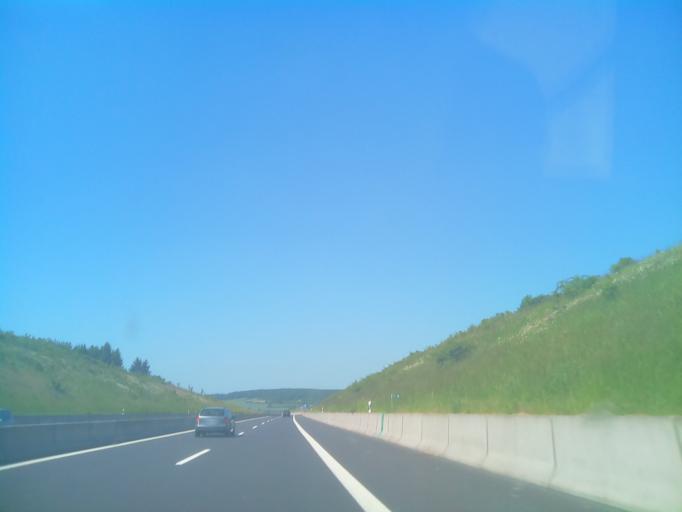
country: DE
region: Bavaria
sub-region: Regierungsbezirk Unterfranken
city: Munnerstadt
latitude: 50.2242
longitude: 10.2188
